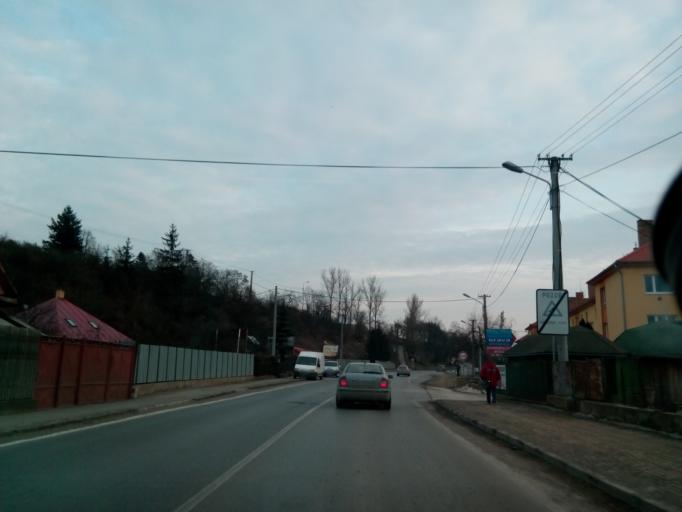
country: SK
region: Presovsky
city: Sabinov
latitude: 49.0995
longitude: 21.1055
